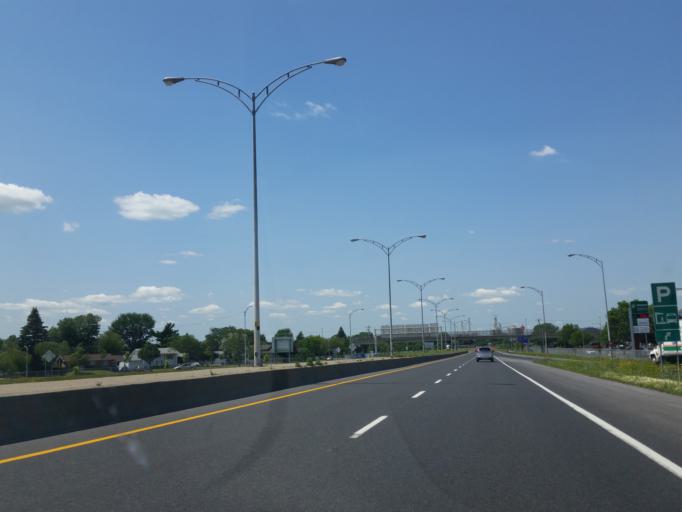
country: CA
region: Quebec
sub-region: Monteregie
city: Saint-Jean-sur-Richelieu
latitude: 45.3269
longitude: -73.2706
